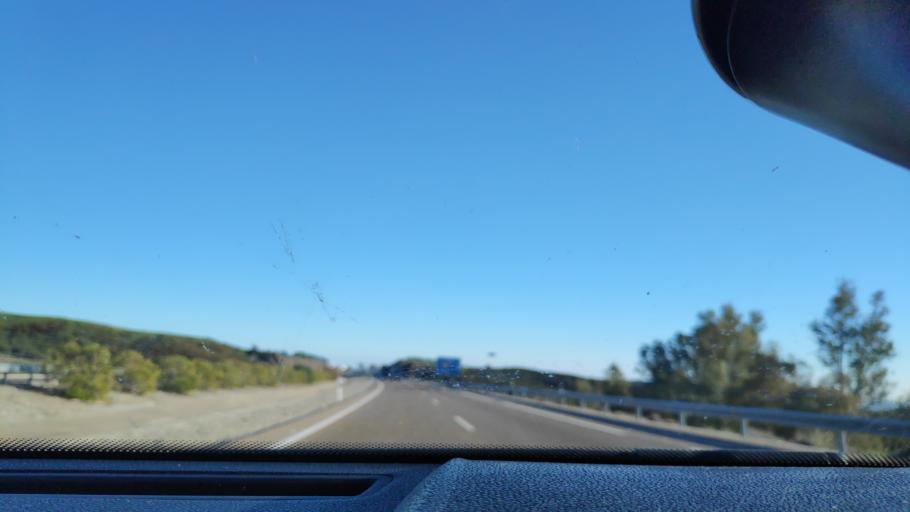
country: ES
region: Andalusia
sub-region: Provincia de Sevilla
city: Gerena
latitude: 37.5795
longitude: -6.1165
